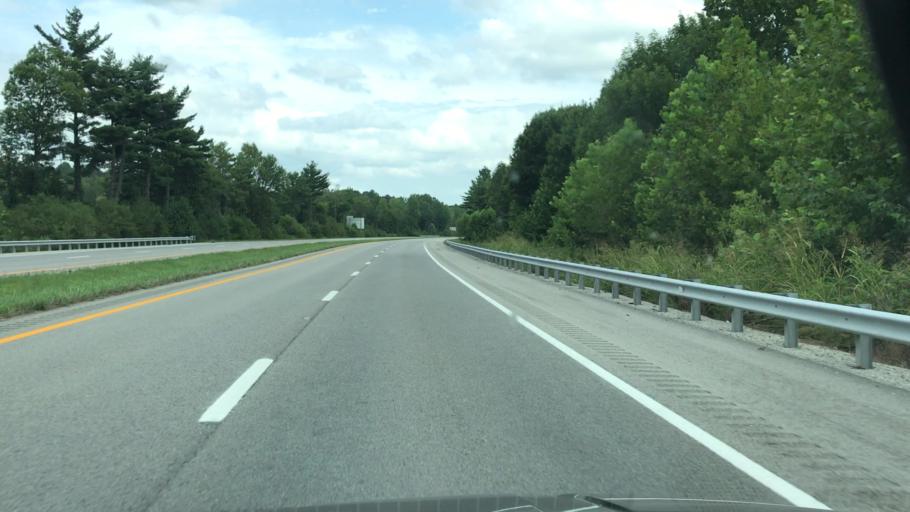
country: US
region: Kentucky
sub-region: Hopkins County
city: Dawson Springs
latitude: 37.1999
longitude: -87.6691
